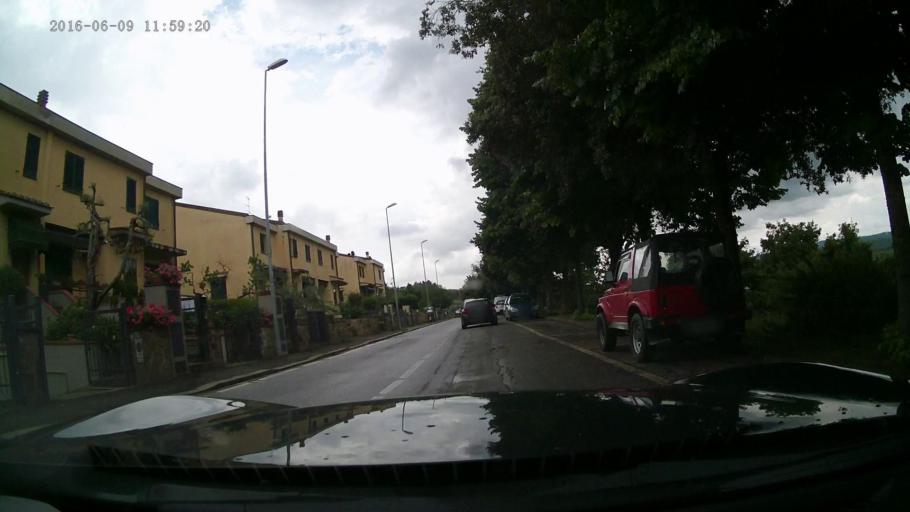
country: IT
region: Tuscany
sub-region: Province of Florence
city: Panzano in Chianti
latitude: 43.5445
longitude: 11.3124
